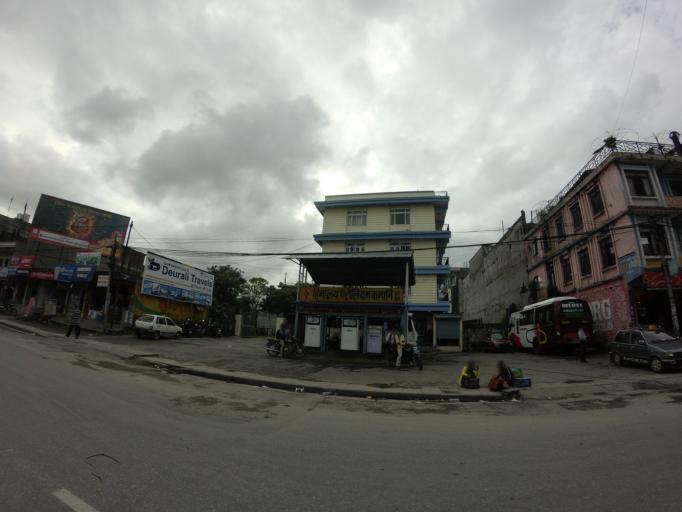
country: NP
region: Western Region
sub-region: Gandaki Zone
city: Pokhara
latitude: 28.2081
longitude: 83.9844
